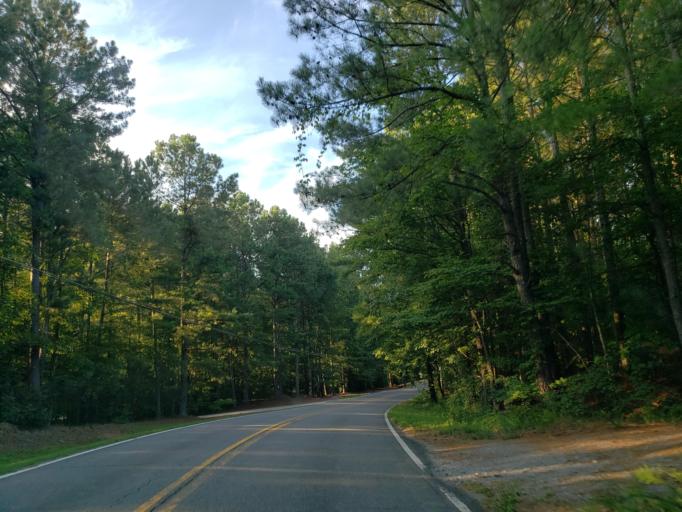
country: US
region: Georgia
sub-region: Bartow County
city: Emerson
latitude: 34.2040
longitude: -84.6927
